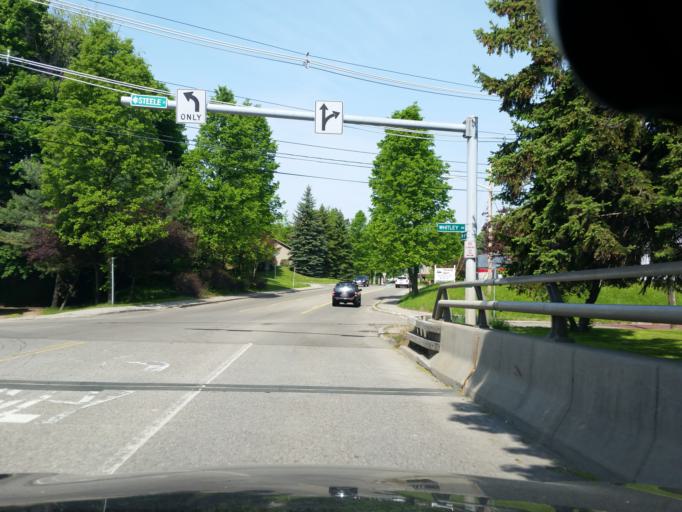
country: US
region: New York
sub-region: Chautauqua County
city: Jamestown
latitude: 42.0975
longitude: -79.2543
